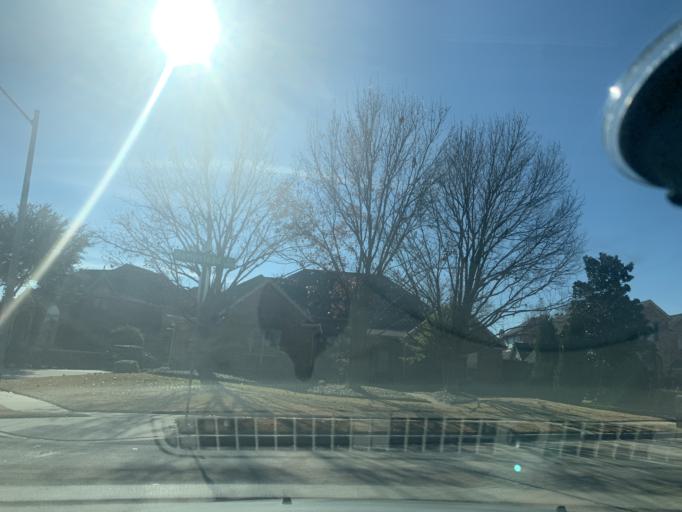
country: US
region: Texas
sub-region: Denton County
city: The Colony
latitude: 33.0530
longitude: -96.8235
